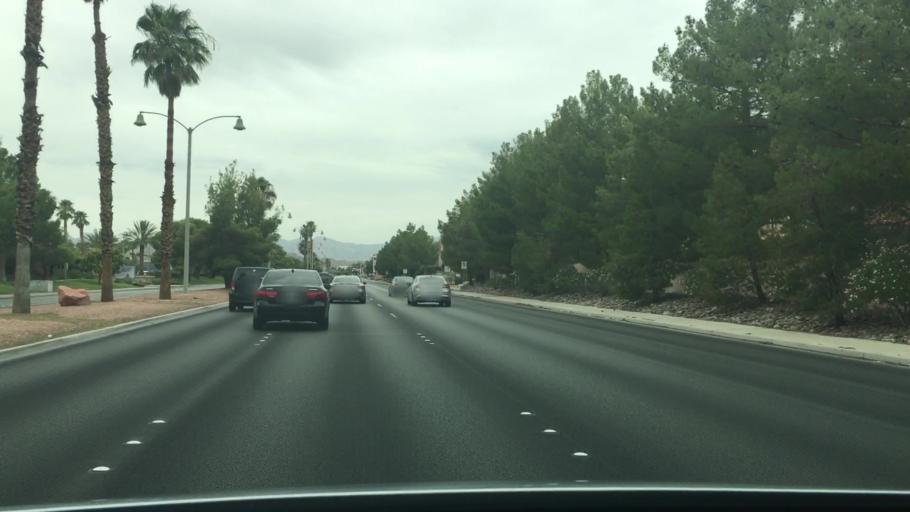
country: US
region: Nevada
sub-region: Clark County
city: Summerlin South
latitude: 36.1443
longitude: -115.2913
